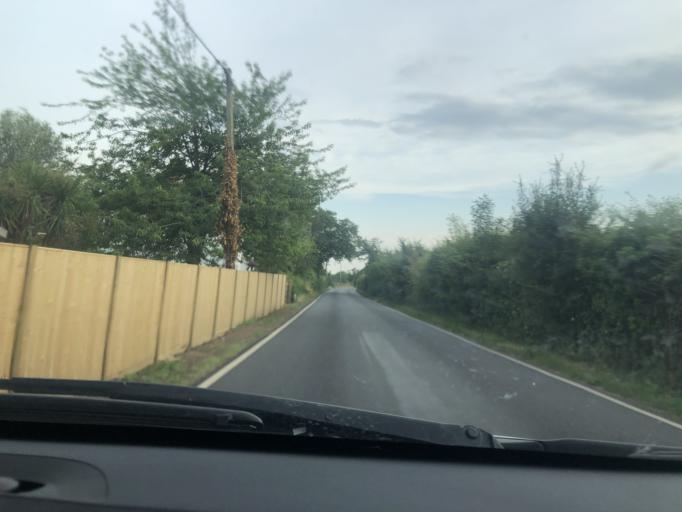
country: GB
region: England
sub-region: Kent
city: Herne Bay
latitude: 51.3371
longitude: 1.1569
